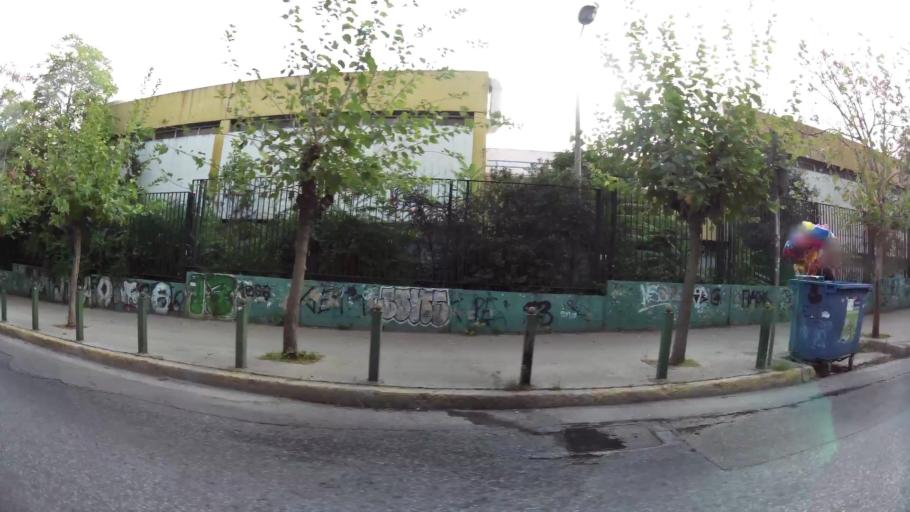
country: GR
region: Attica
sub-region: Nomarchia Athinas
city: Kipseli
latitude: 38.0125
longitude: 23.7391
